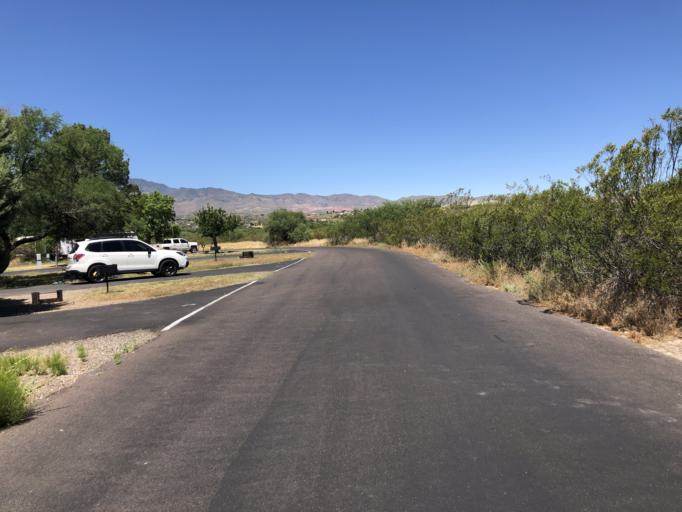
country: US
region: Arizona
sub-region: Yavapai County
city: Cottonwood
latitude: 34.7552
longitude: -112.0167
